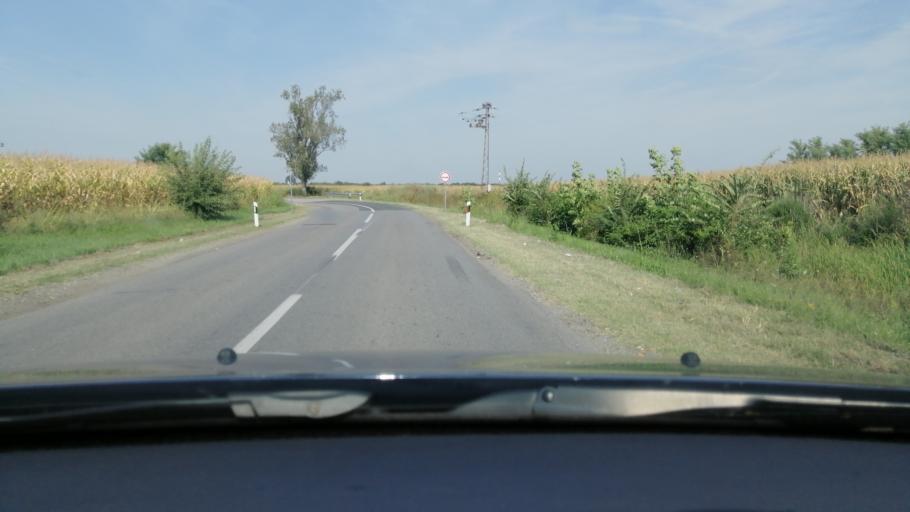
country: RS
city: Ecka
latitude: 45.3211
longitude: 20.4590
